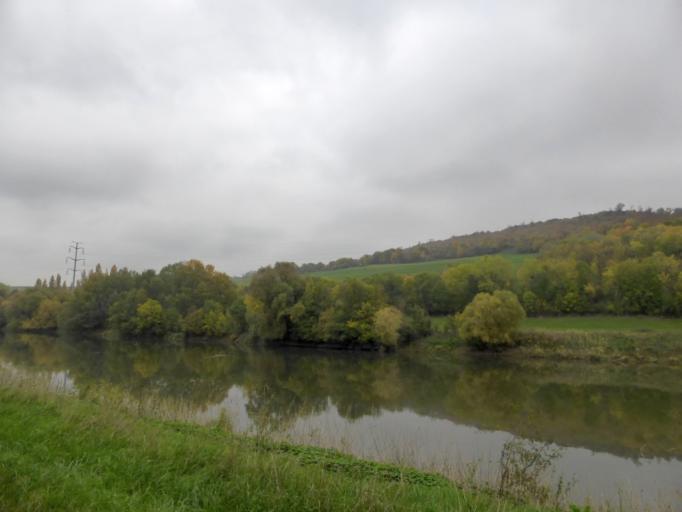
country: FR
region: Lorraine
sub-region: Departement de Meurthe-et-Moselle
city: Frouard
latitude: 48.7694
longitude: 6.1400
